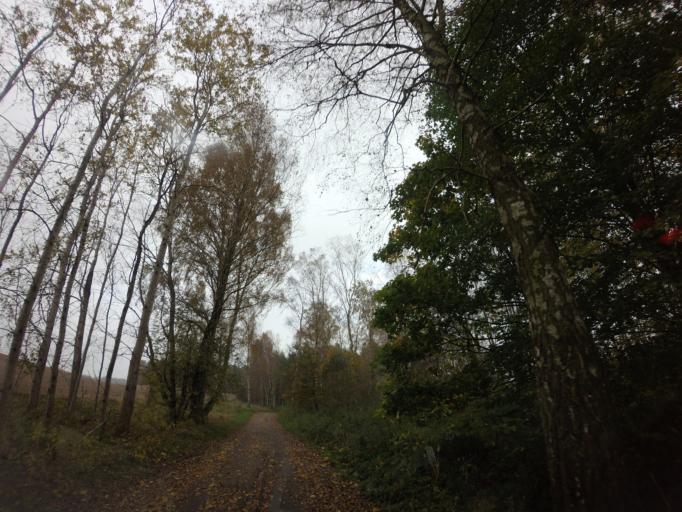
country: PL
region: West Pomeranian Voivodeship
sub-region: Powiat choszczenski
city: Recz
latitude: 53.2391
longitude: 15.5498
